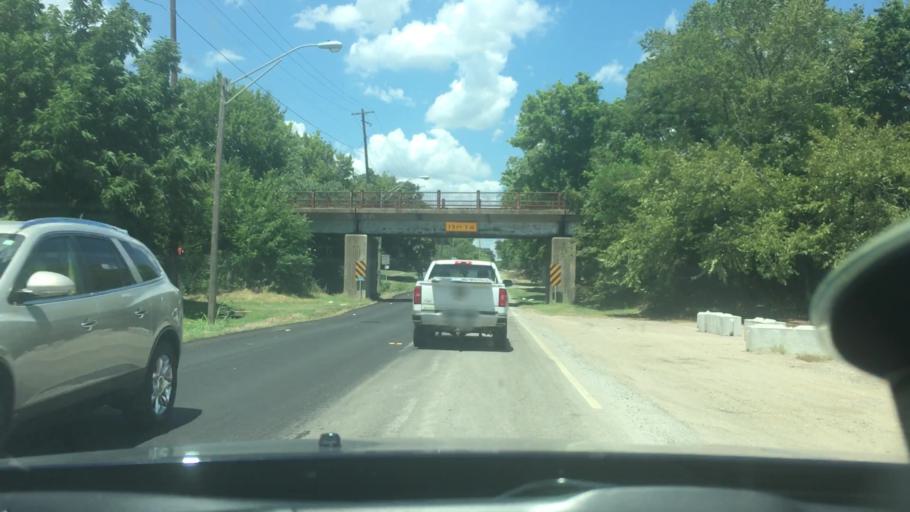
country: US
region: Oklahoma
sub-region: Bryan County
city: Durant
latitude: 33.9873
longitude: -96.3708
